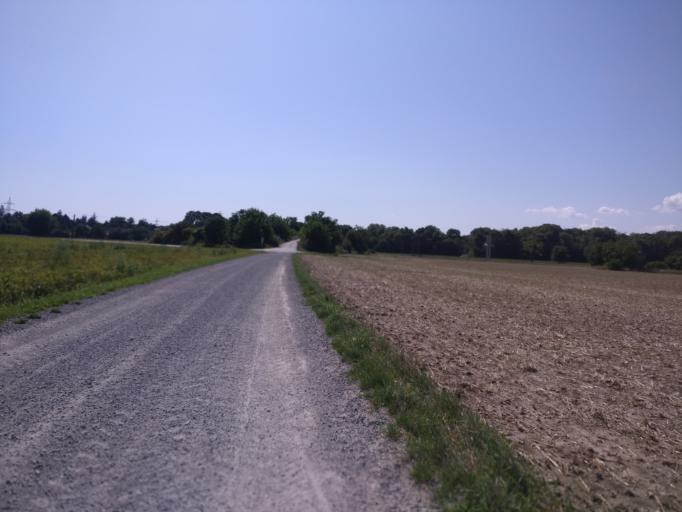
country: AT
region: Lower Austria
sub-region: Politischer Bezirk Wiener Neustadt
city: Ebenfurth
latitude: 47.8749
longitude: 16.3414
